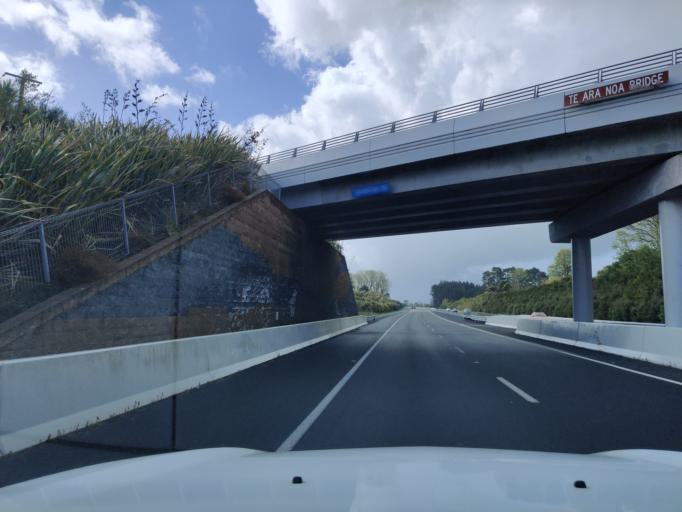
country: NZ
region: Waikato
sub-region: Waipa District
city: Cambridge
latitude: -37.8842
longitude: 175.4924
